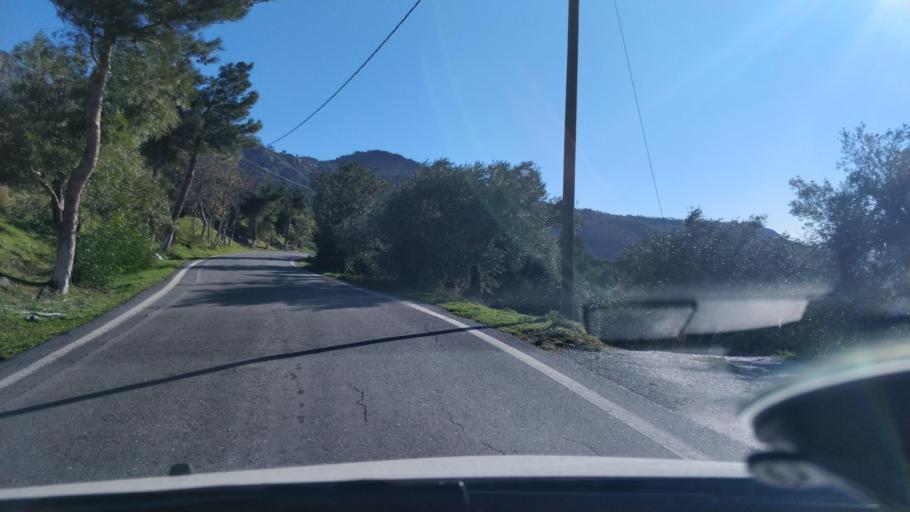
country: GR
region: Crete
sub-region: Nomos Lasithiou
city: Kritsa
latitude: 35.0798
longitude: 25.5899
